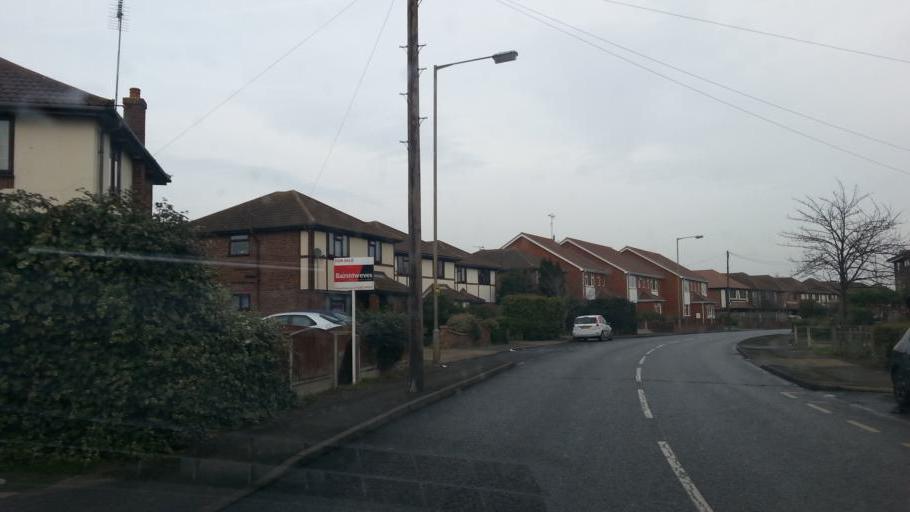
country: GB
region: England
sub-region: Essex
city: Canvey Island
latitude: 51.5286
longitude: 0.5756
